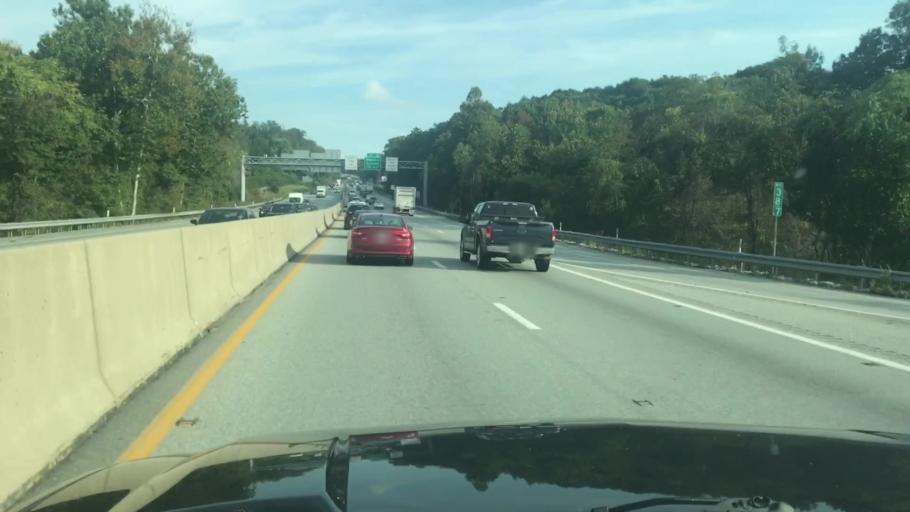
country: US
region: Pennsylvania
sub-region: Cumberland County
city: New Cumberland
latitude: 40.2057
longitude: -76.8739
